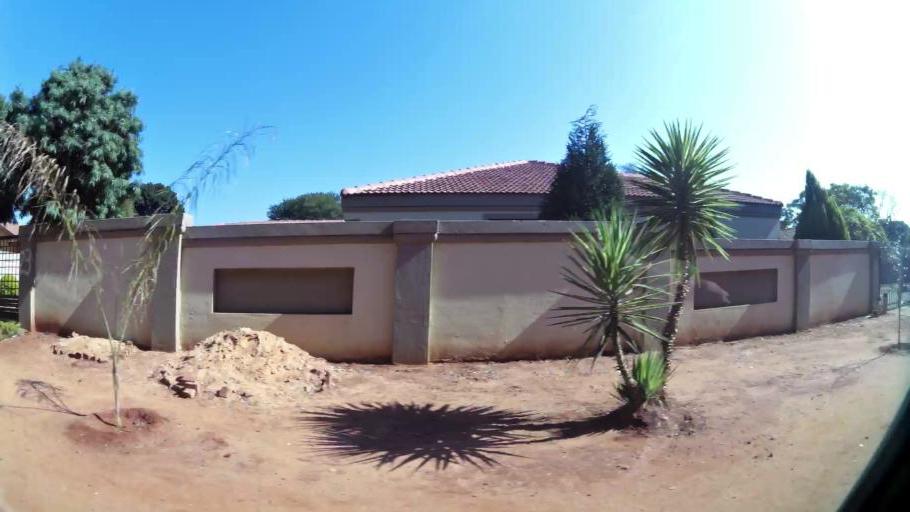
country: ZA
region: North-West
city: Ga-Rankuwa
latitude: -25.6450
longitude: 28.0986
